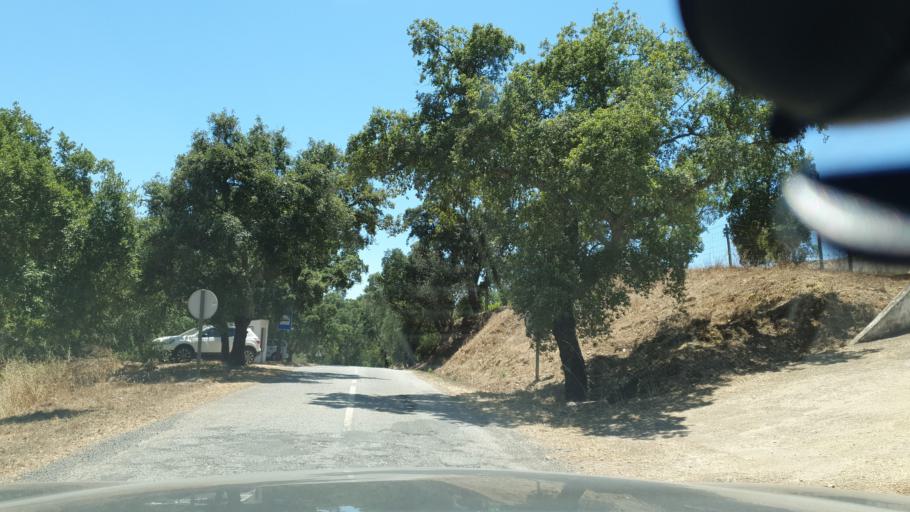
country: PT
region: Beja
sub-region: Odemira
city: Odemira
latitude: 37.6153
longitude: -8.5025
